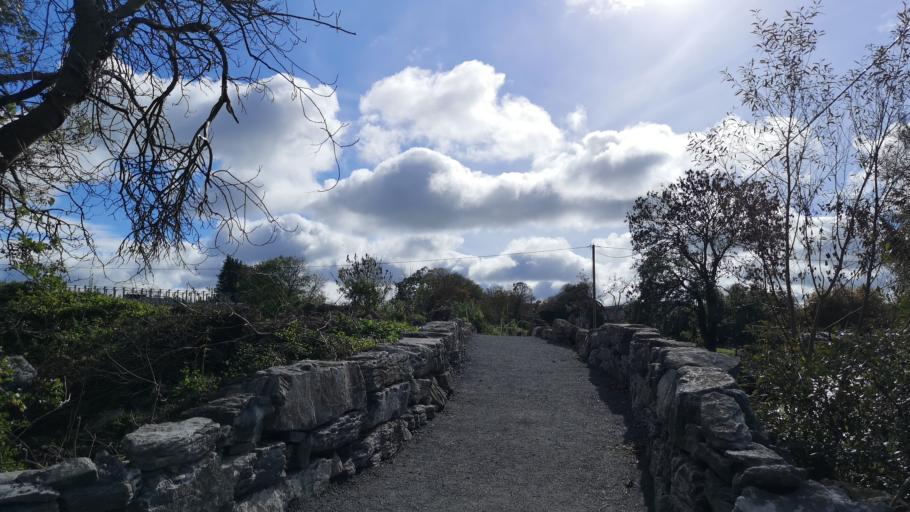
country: IE
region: Connaught
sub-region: County Galway
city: Gort
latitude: 53.0681
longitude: -8.8164
